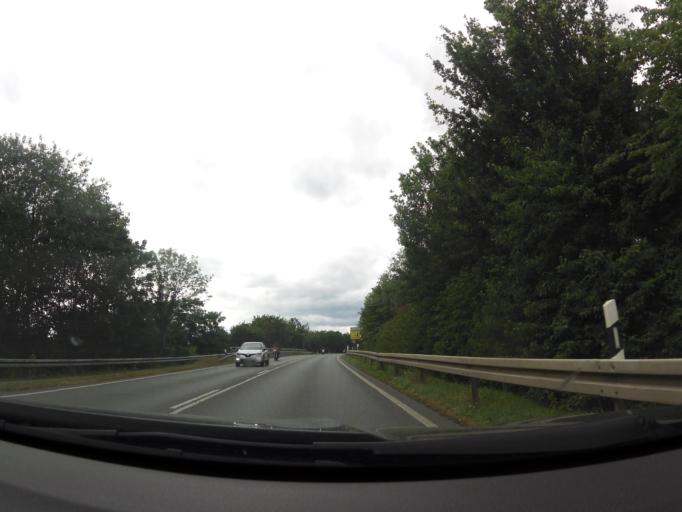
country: DE
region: North Rhine-Westphalia
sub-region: Regierungsbezirk Dusseldorf
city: Wesel
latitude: 51.6400
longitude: 6.6386
